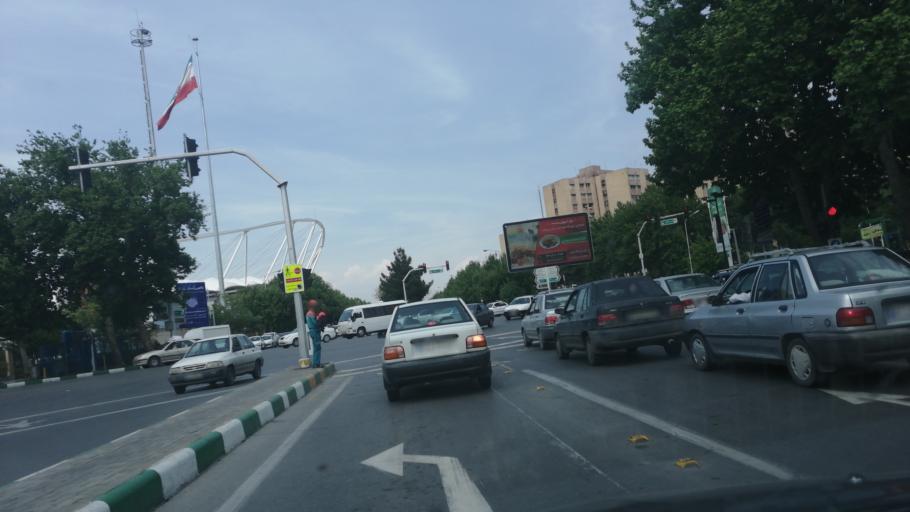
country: IR
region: Razavi Khorasan
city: Mashhad
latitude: 36.3238
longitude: 59.5697
